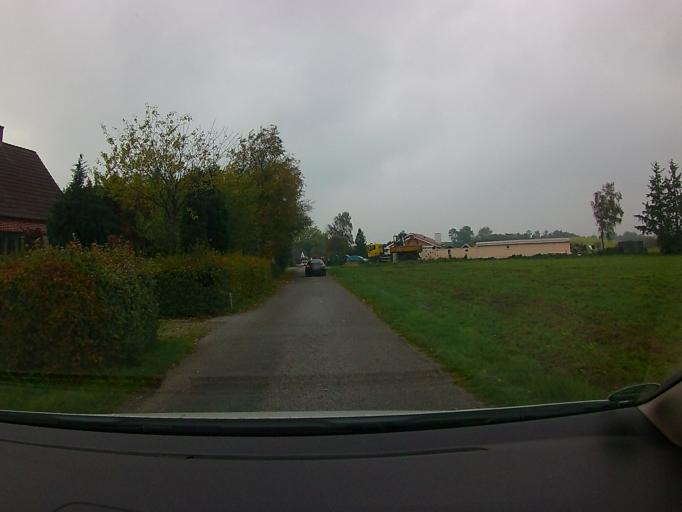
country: DK
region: South Denmark
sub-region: Aabenraa Kommune
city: Krusa
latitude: 54.8661
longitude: 9.4567
